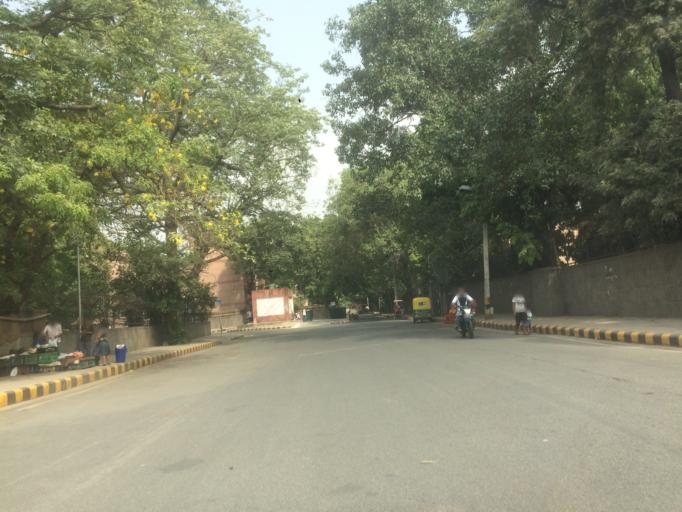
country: IN
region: NCT
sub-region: New Delhi
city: New Delhi
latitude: 28.6381
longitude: 77.2054
